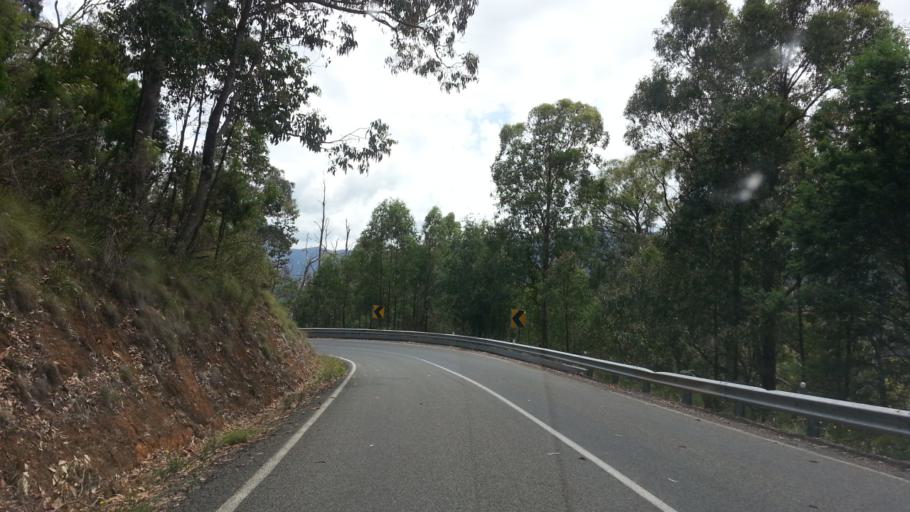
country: AU
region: Victoria
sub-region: Alpine
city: Mount Beauty
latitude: -36.7398
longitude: 147.1903
